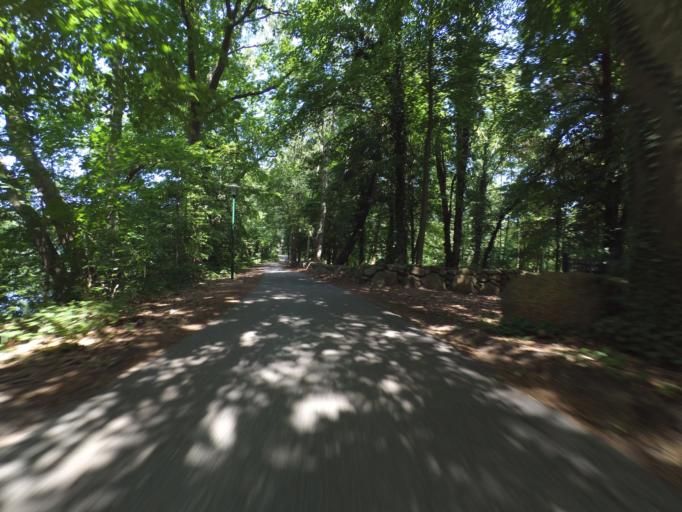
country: DE
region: Mecklenburg-Vorpommern
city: Plau am See
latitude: 53.4359
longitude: 12.2842
